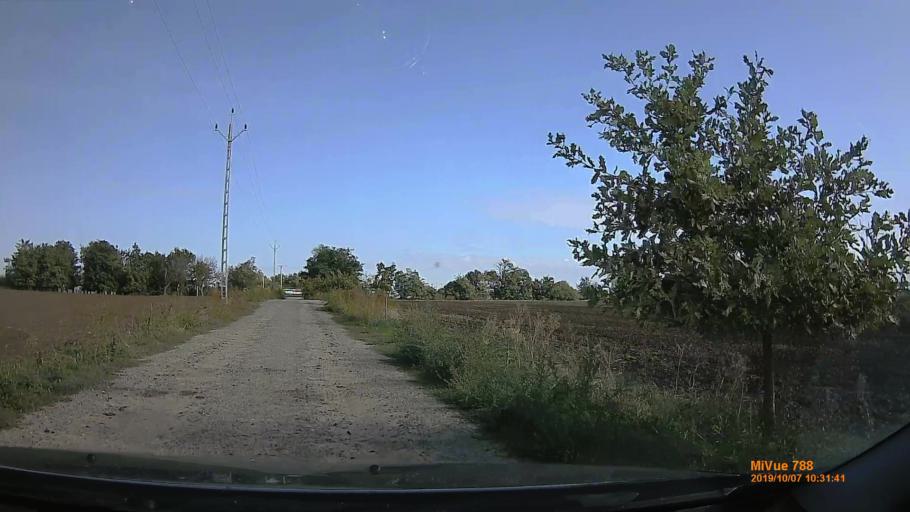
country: HU
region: Bekes
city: Kondoros
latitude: 46.7465
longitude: 20.8448
